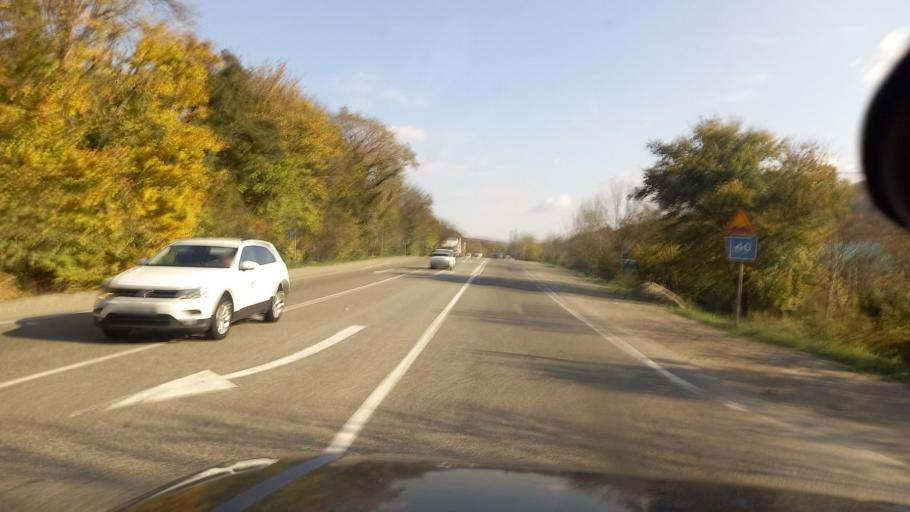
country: RU
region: Krasnodarskiy
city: Verkhnebakanskiy
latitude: 44.8478
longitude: 37.7206
